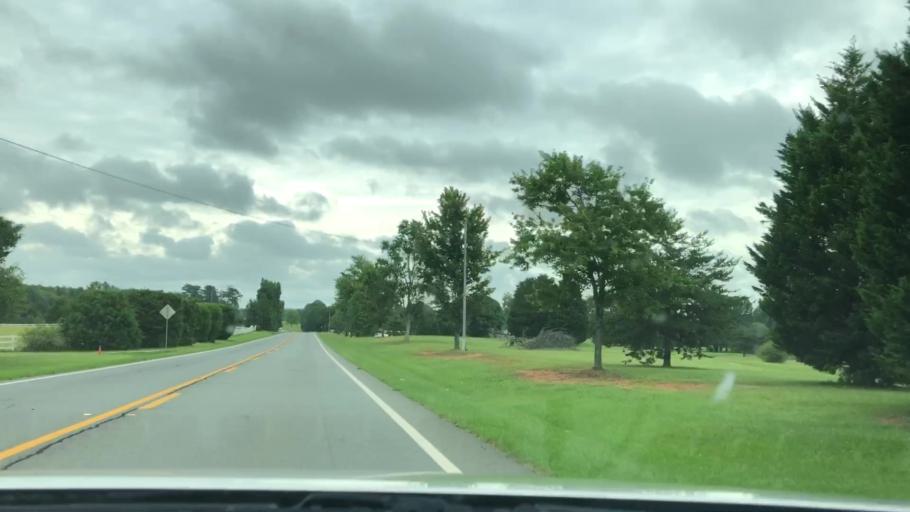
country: US
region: Georgia
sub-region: Pike County
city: Zebulon
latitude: 33.1107
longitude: -84.3921
